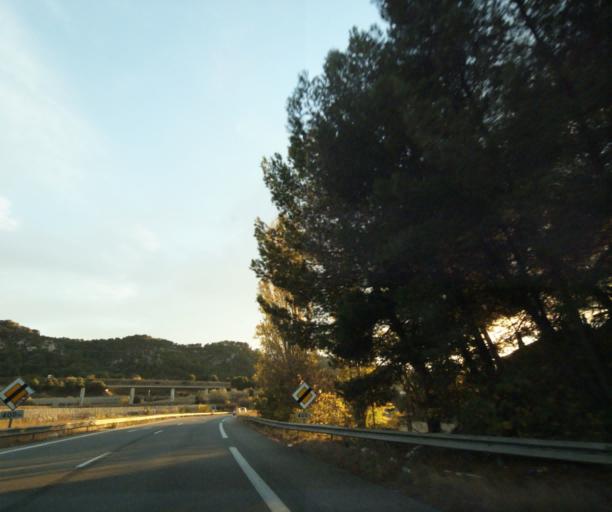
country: FR
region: Provence-Alpes-Cote d'Azur
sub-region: Departement des Bouches-du-Rhone
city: Les Pennes-Mirabeau
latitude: 43.4023
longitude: 5.2961
